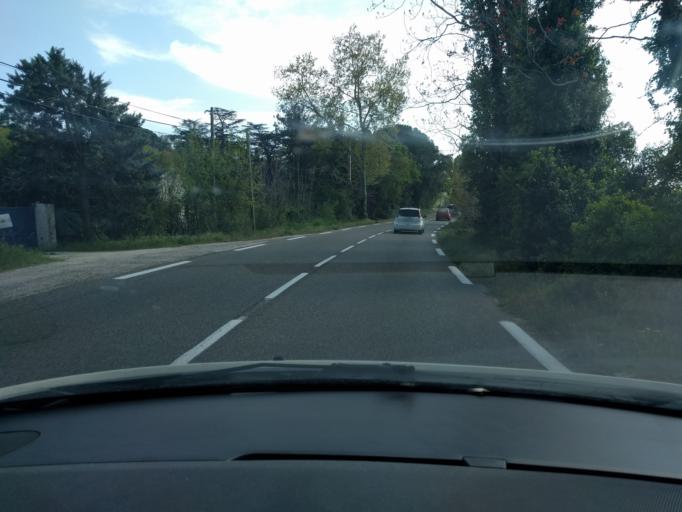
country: FR
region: Provence-Alpes-Cote d'Azur
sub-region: Departement du Var
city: Pierrefeu-du-Var
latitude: 43.1991
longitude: 6.1340
